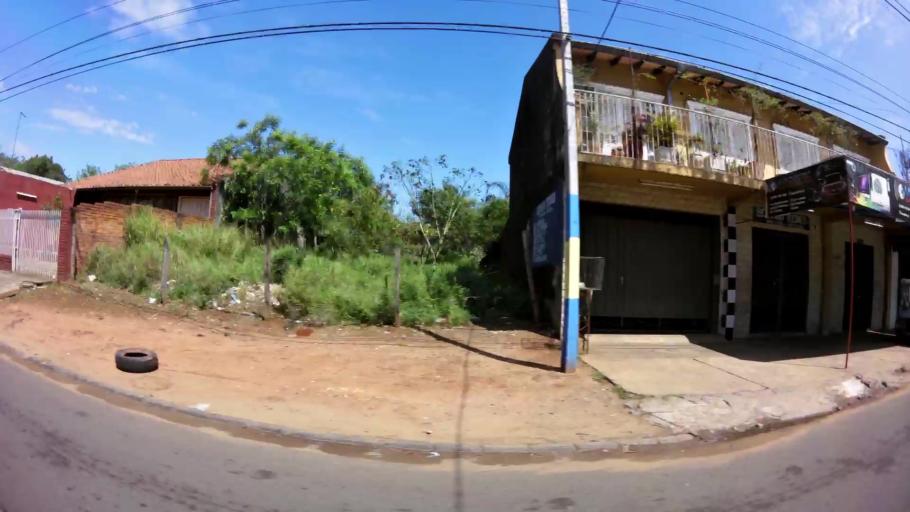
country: PY
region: Central
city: San Lorenzo
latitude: -25.3034
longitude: -57.5044
